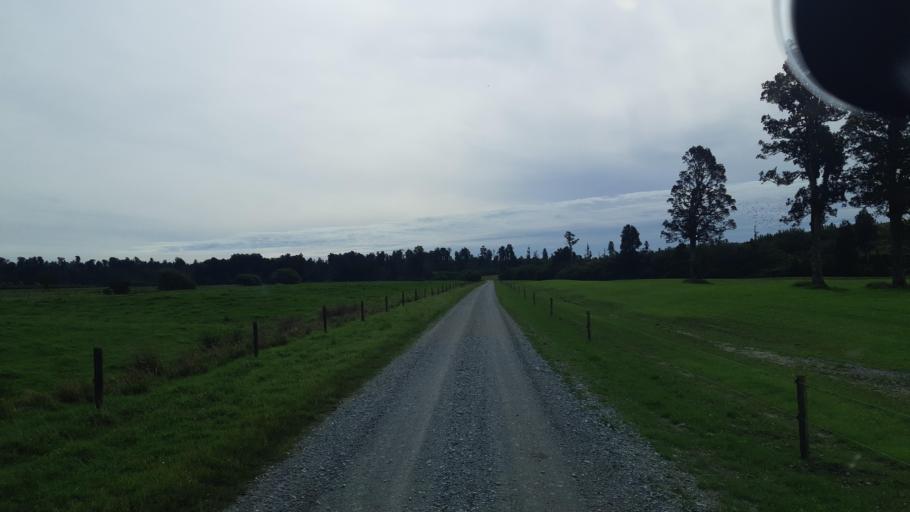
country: NZ
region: West Coast
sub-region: Westland District
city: Hokitika
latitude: -43.1141
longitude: 170.4836
